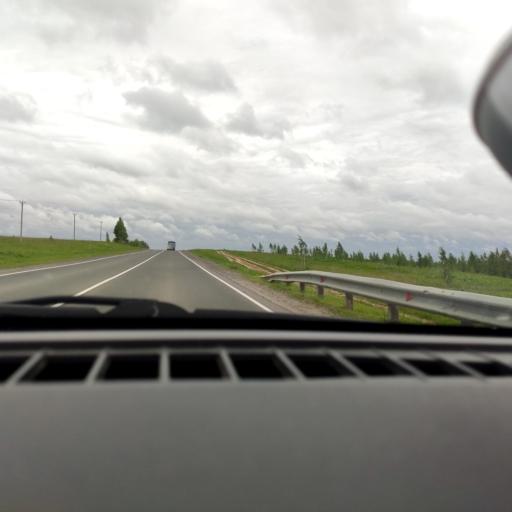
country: RU
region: Perm
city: Ust'-Kachka
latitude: 57.9505
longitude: 55.7362
